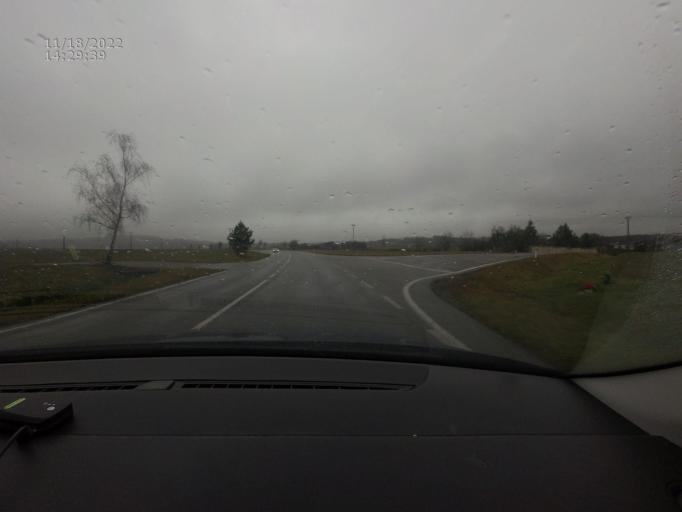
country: CZ
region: Jihocesky
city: Kovarov
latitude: 49.4362
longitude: 14.2425
